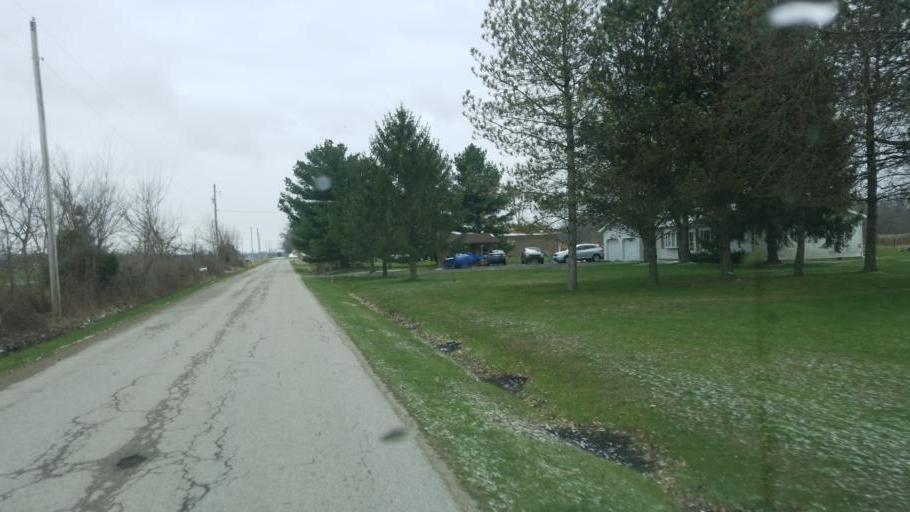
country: US
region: Ohio
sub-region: Morrow County
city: Cardington
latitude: 40.5224
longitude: -82.9485
